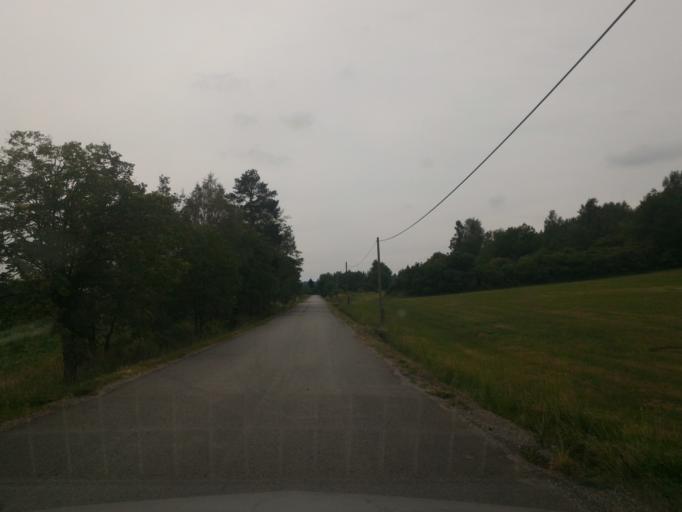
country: CZ
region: Vysocina
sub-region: Okres Jihlava
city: Telc
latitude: 49.1997
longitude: 15.3835
